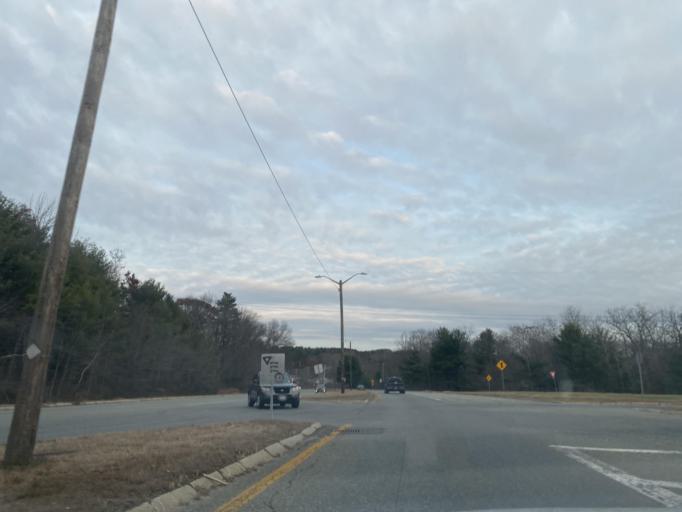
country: US
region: Massachusetts
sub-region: Worcester County
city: East Brookfield
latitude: 42.2314
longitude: -72.0195
